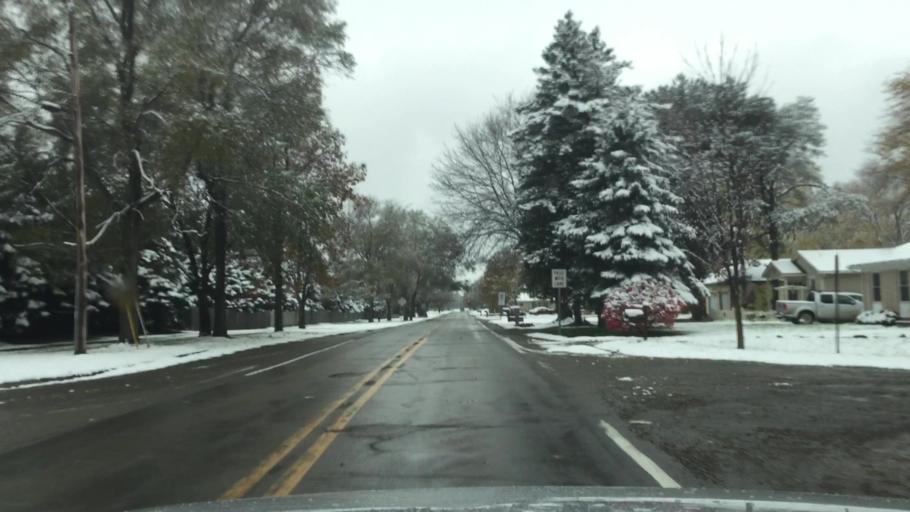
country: US
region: Michigan
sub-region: Oakland County
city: Oxford
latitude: 42.8094
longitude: -83.2873
